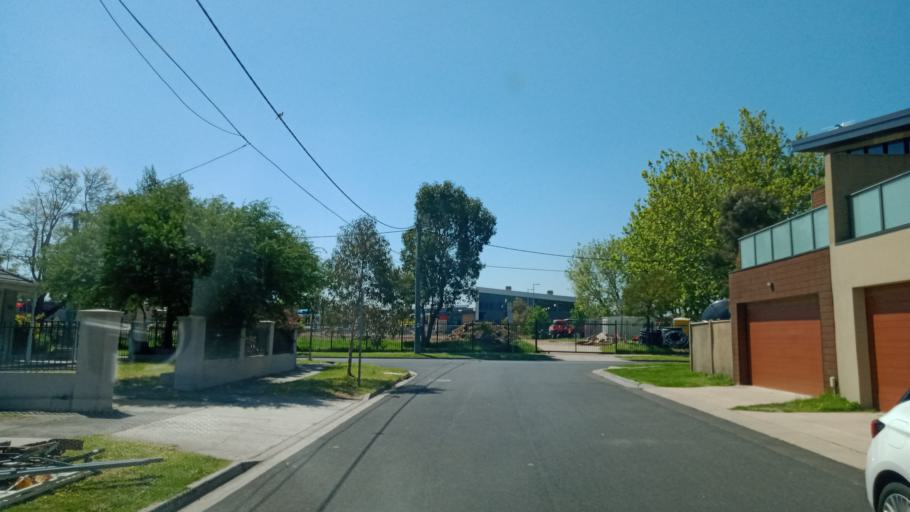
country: AU
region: Victoria
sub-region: Monash
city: Oakleigh South
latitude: -37.9216
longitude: 145.0732
